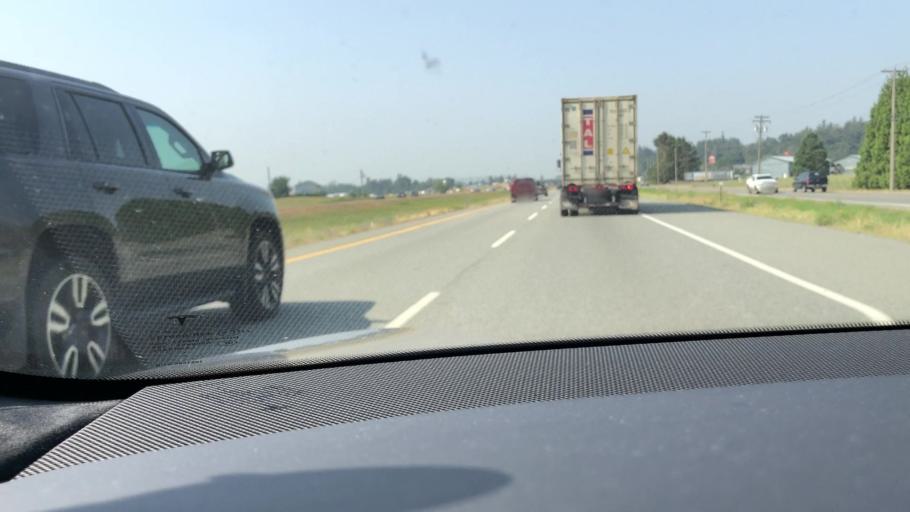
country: CA
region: British Columbia
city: Abbotsford
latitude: 49.0425
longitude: -122.2100
